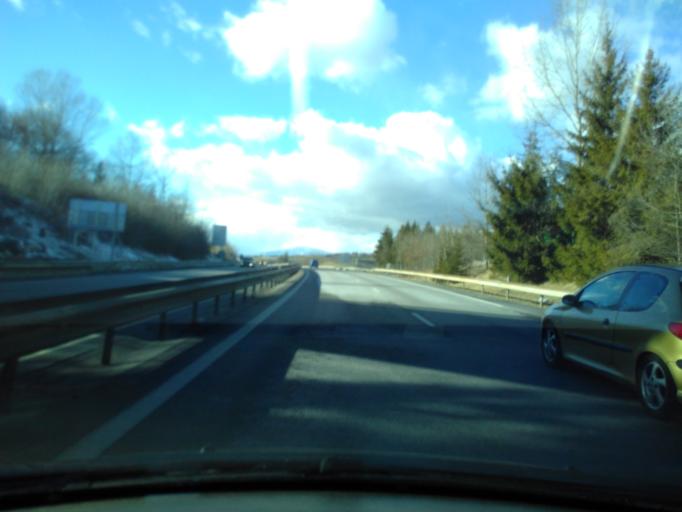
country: FR
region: Rhone-Alpes
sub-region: Departement de la Haute-Savoie
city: Allonzier-la-Caille
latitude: 46.0010
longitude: 6.1468
